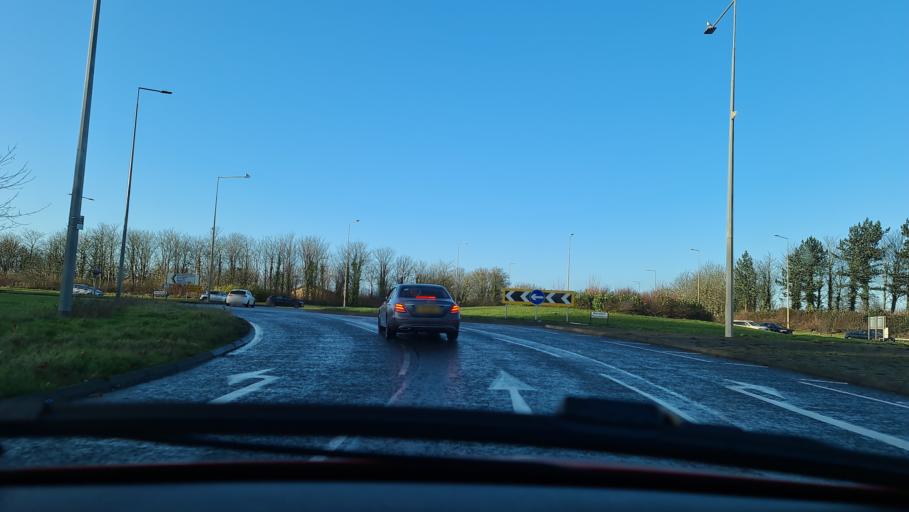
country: GB
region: England
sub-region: Milton Keynes
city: Milton Keynes
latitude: 52.0487
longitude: -0.7511
